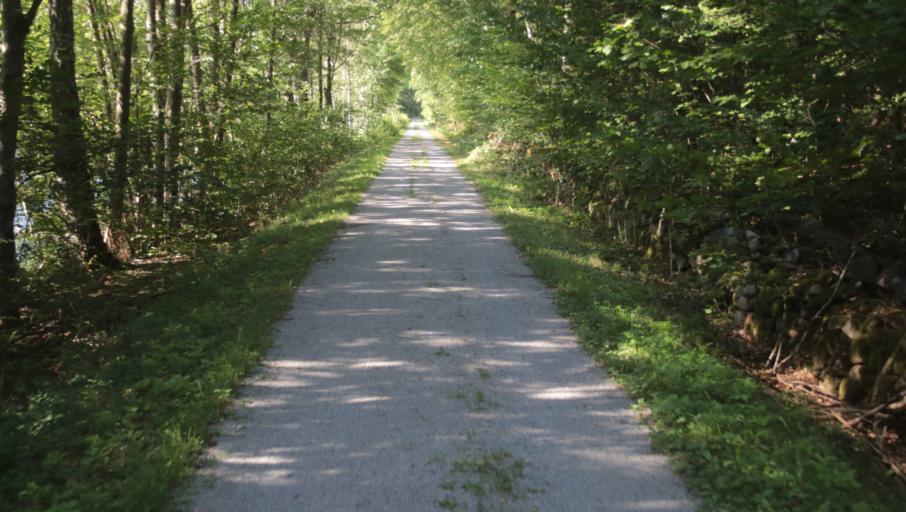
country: SE
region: Blekinge
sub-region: Karlshamns Kommun
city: Svangsta
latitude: 56.3706
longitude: 14.6834
